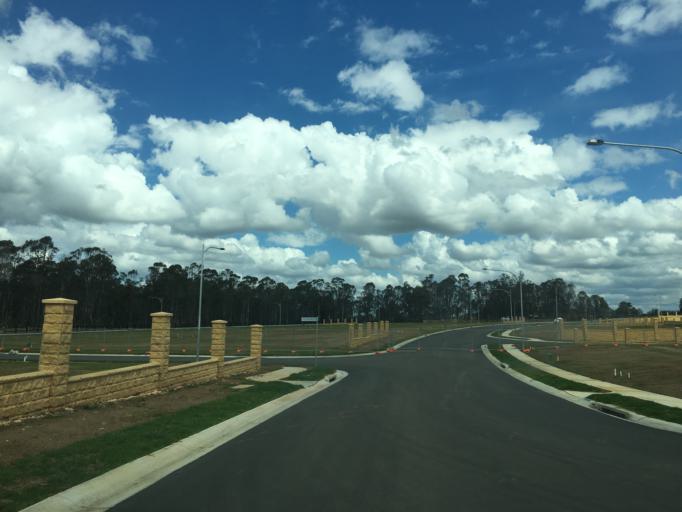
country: AU
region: New South Wales
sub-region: Campbelltown Municipality
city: Denham Court
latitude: -33.9899
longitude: 150.8010
